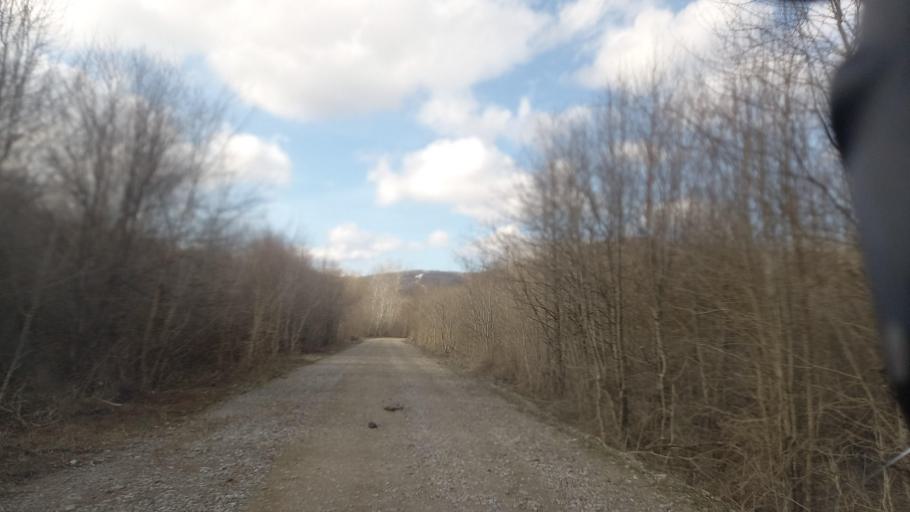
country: RU
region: Krasnodarskiy
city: Smolenskaya
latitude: 44.6169
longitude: 38.8288
